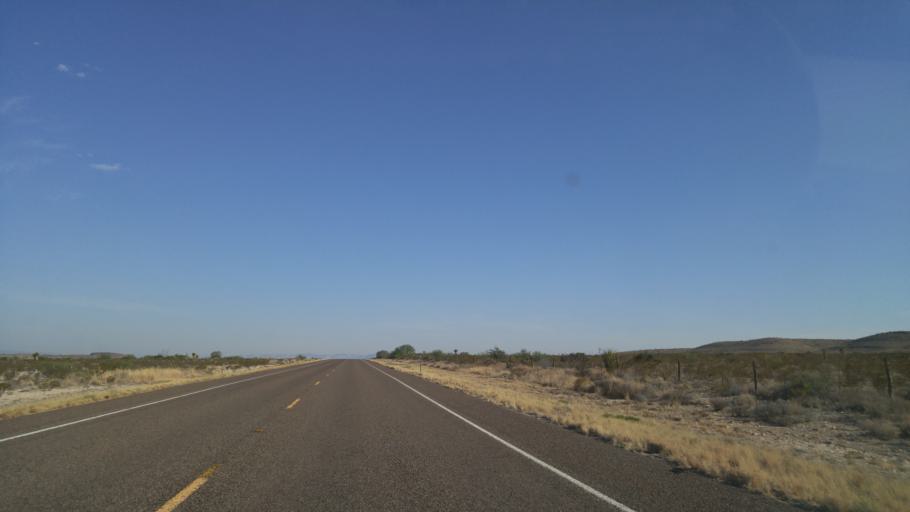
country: US
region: Texas
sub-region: Brewster County
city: Alpine
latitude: 29.7582
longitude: -103.5712
